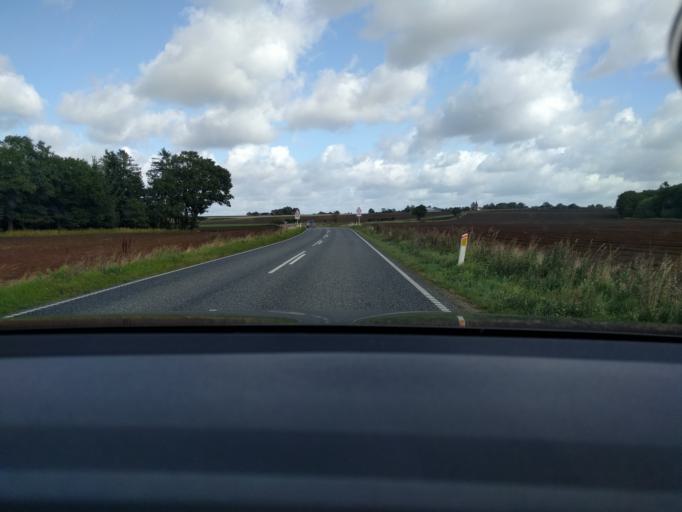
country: DK
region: Central Jutland
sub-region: Viborg Kommune
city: Bjerringbro
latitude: 56.3030
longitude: 9.6967
